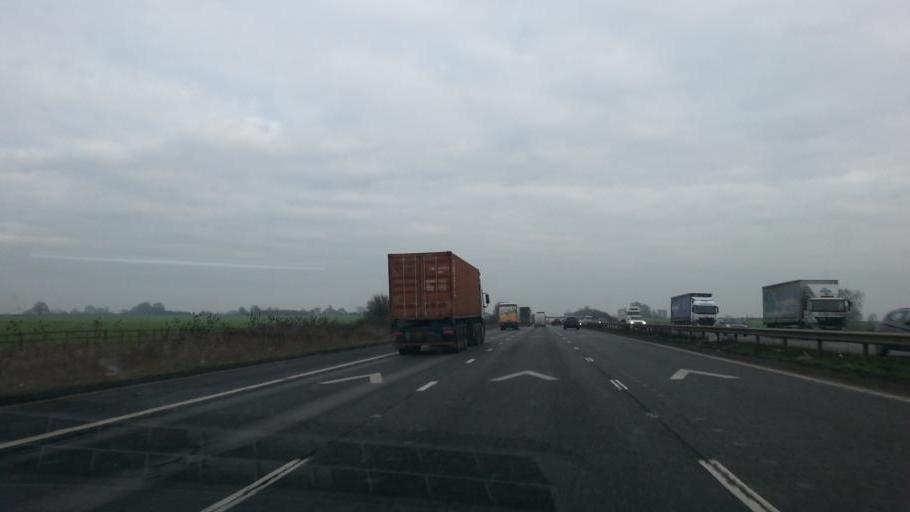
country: GB
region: England
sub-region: Warwickshire
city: Brandon
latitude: 52.4362
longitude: -1.3785
